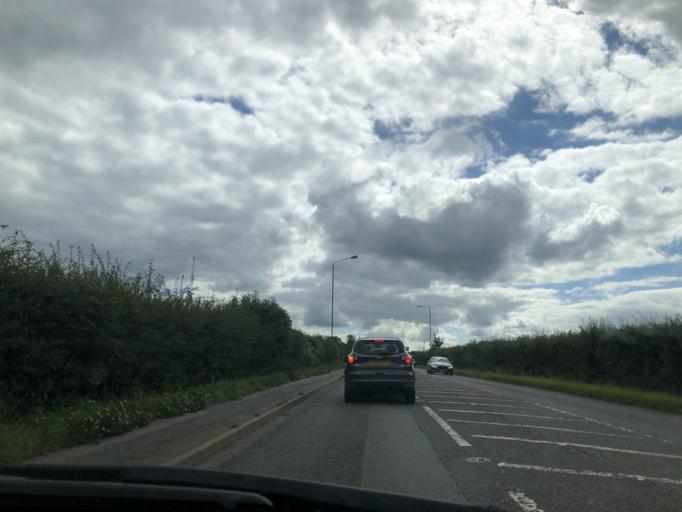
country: GB
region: England
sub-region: Kent
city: Halstead
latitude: 51.3308
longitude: 0.1497
